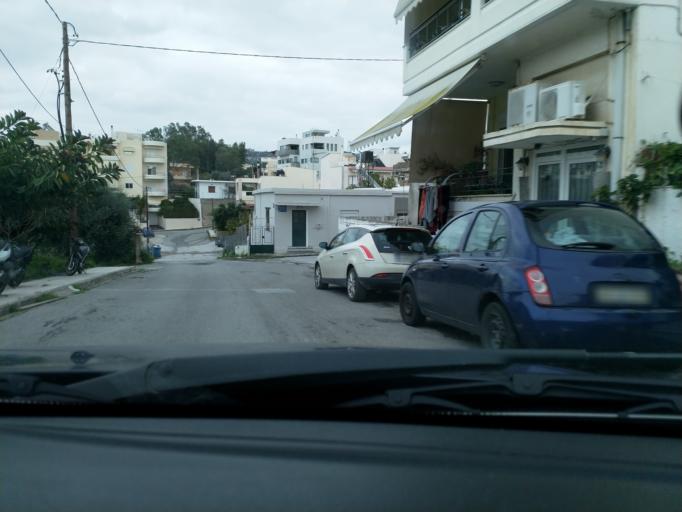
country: GR
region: Crete
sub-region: Nomos Chanias
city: Chania
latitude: 35.5111
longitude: 24.0401
